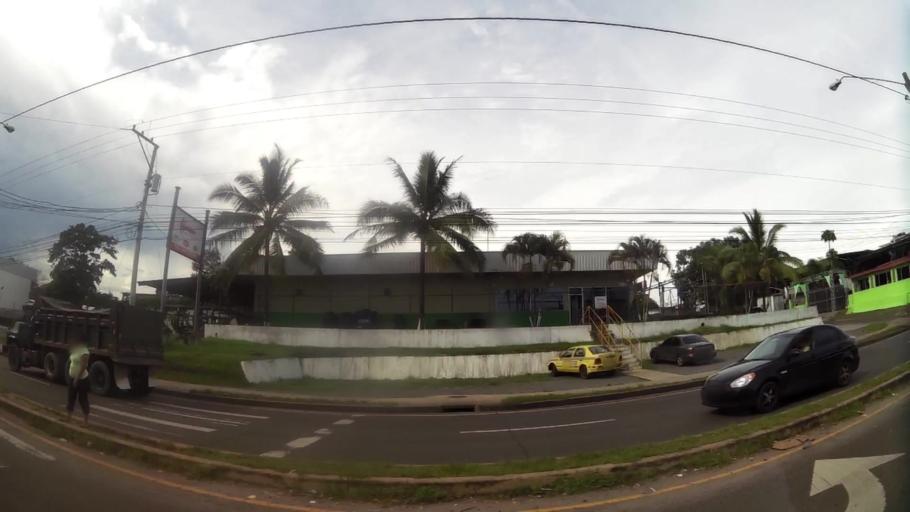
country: PA
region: Panama
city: El Coco
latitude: 8.8722
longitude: -79.7990
